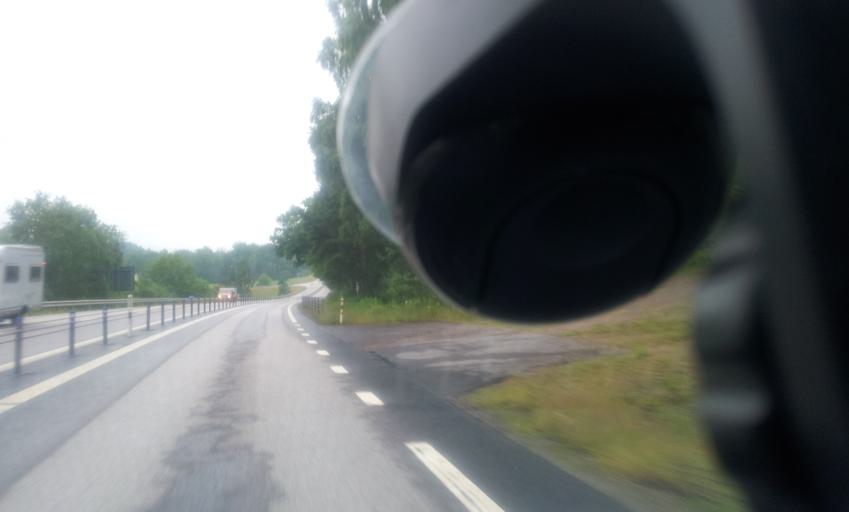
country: SE
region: Kalmar
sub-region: Vasterviks Kommun
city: Gamleby
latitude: 57.8949
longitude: 16.3866
